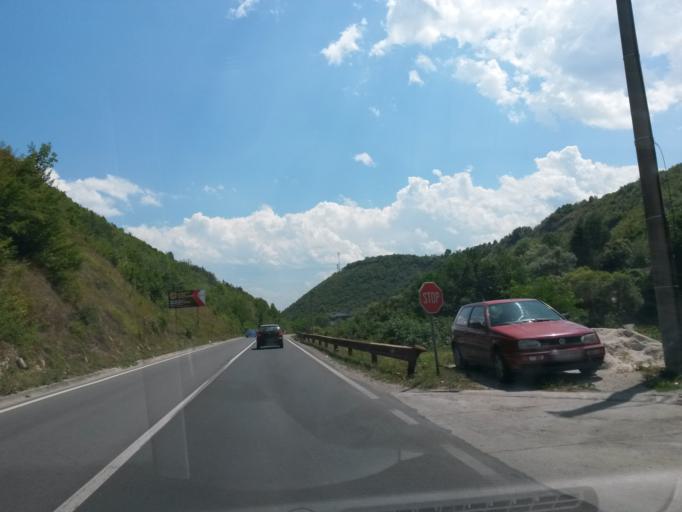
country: BA
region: Federation of Bosnia and Herzegovina
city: Travnik
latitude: 44.2269
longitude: 17.6816
